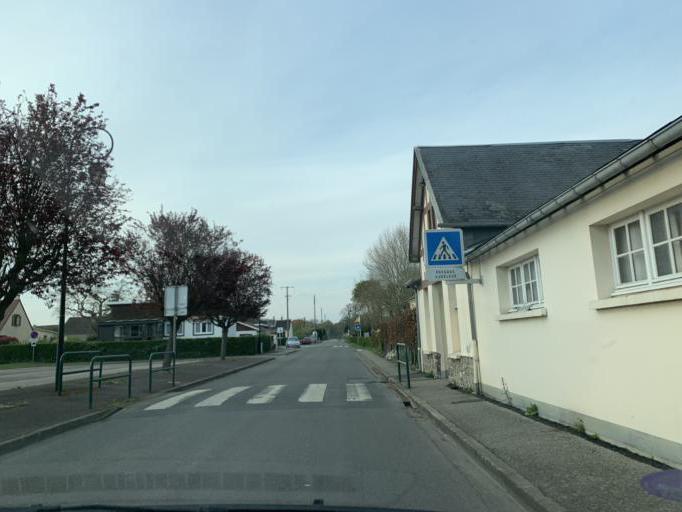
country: FR
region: Haute-Normandie
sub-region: Departement de la Seine-Maritime
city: La Mailleraye-sur-Seine
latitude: 49.4836
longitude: 0.7708
